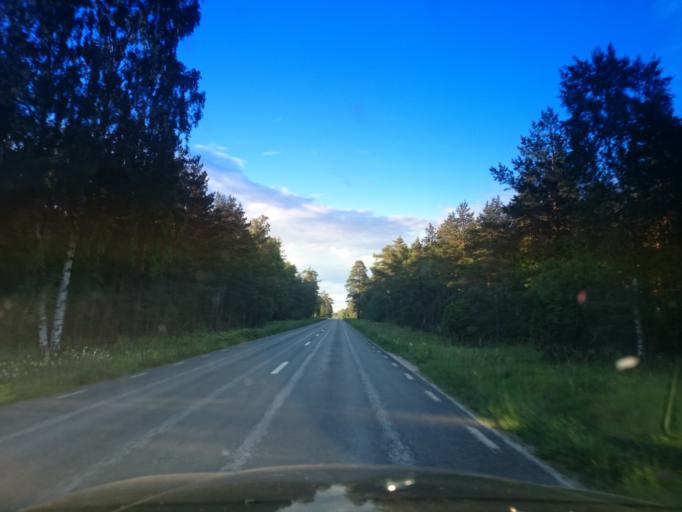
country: SE
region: Gotland
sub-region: Gotland
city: Hemse
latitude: 57.3439
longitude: 18.3806
